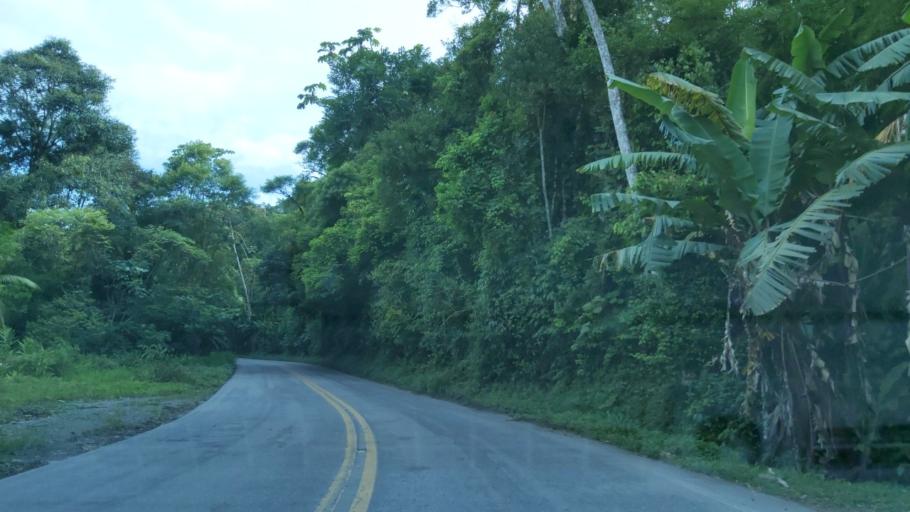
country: BR
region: Sao Paulo
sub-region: Miracatu
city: Miracatu
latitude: -24.0402
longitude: -47.5672
